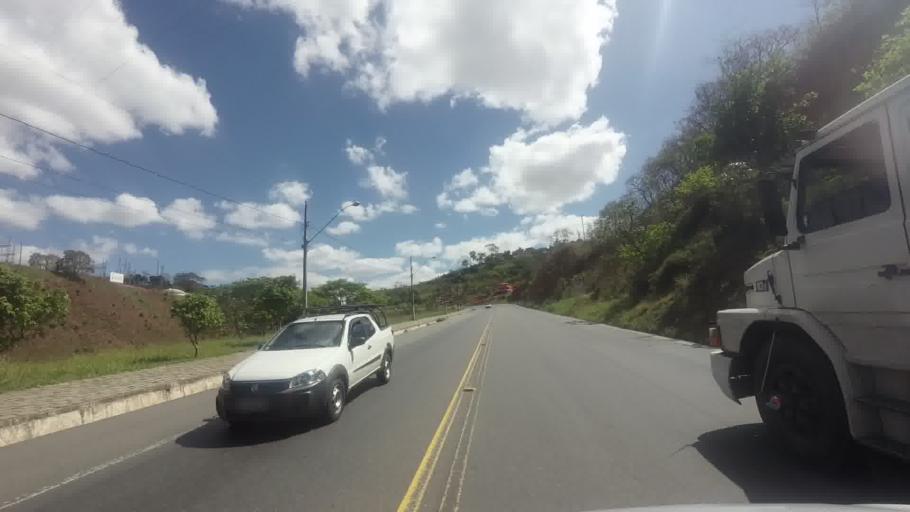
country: BR
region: Minas Gerais
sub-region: Alem Paraiba
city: Alem Paraiba
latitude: -21.8680
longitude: -42.6711
